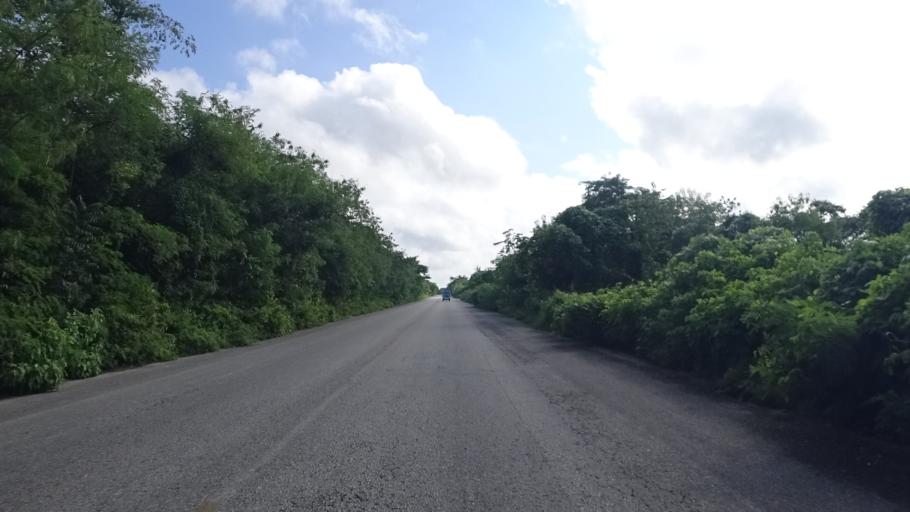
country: MX
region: Yucatan
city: Valladolid
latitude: 20.7184
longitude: -88.2254
